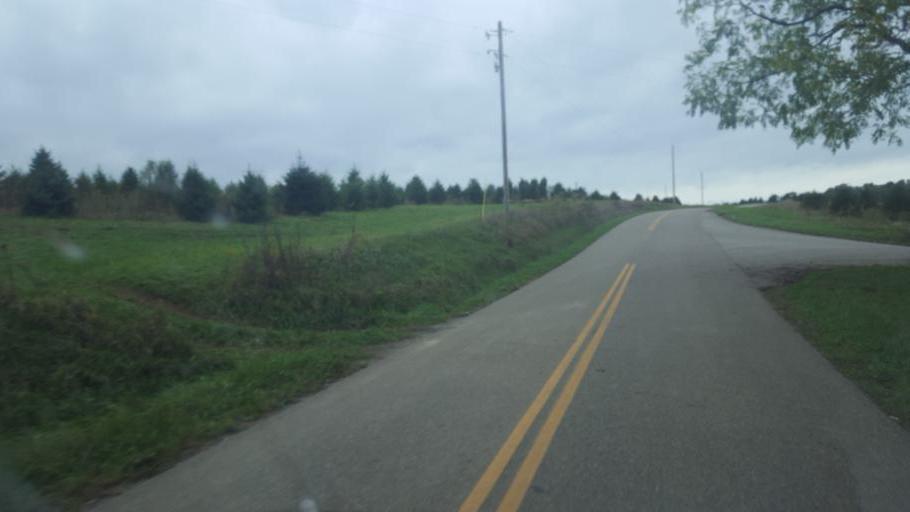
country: US
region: Ohio
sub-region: Carroll County
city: Carrollton
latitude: 40.4746
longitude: -81.0420
